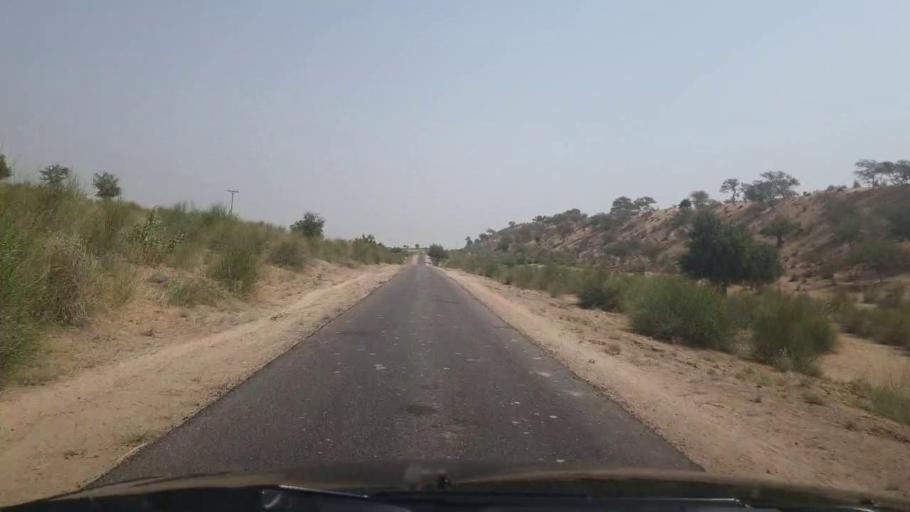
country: PK
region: Sindh
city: Islamkot
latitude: 24.9453
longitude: 70.4147
